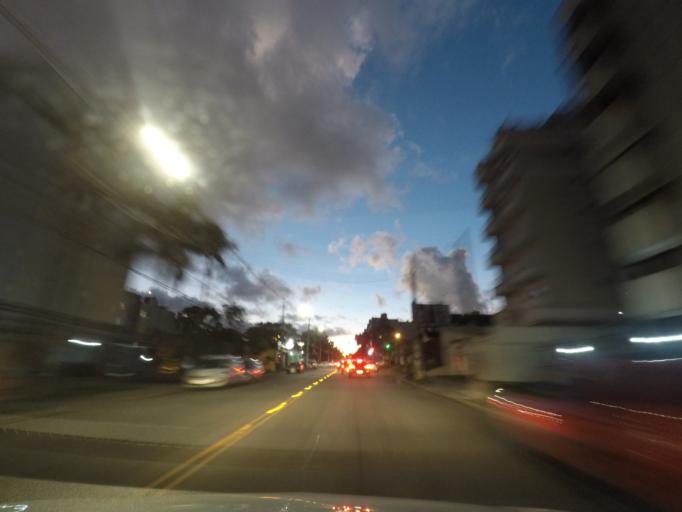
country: BR
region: Parana
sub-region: Curitiba
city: Curitiba
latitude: -25.4607
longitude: -49.2790
